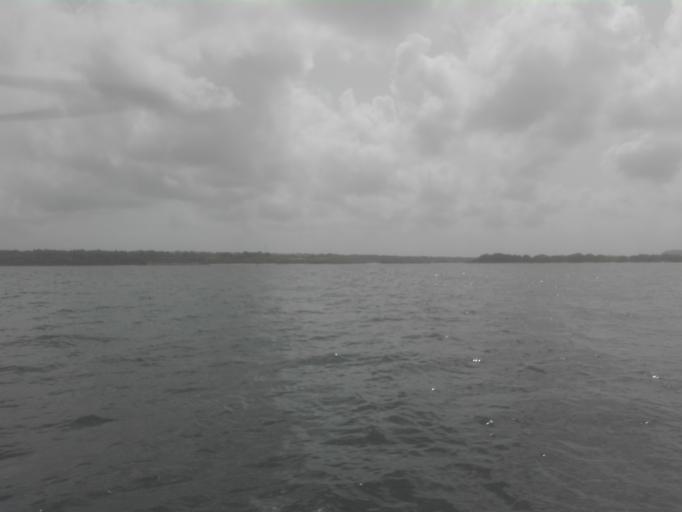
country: CO
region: Bolivar
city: Turbana
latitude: 10.2330
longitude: -75.6132
